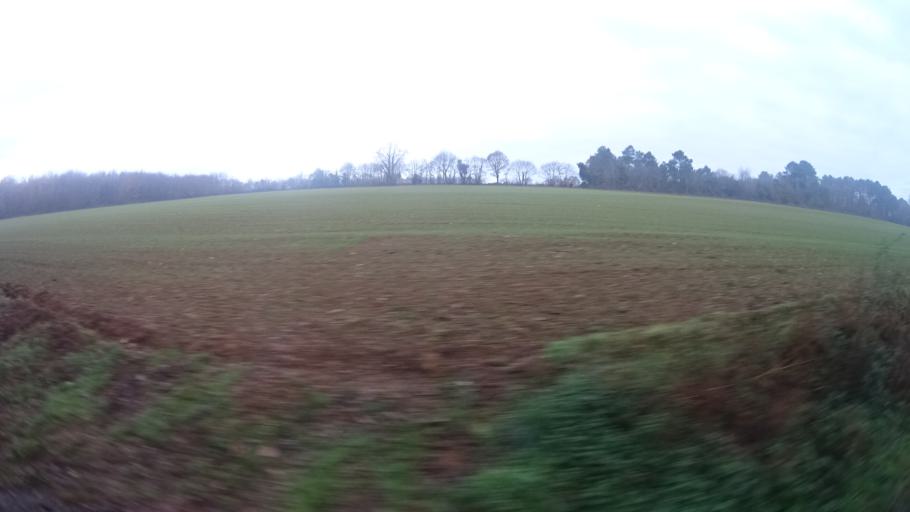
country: FR
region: Pays de la Loire
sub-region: Departement de la Loire-Atlantique
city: Avessac
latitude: 47.6505
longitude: -2.0172
